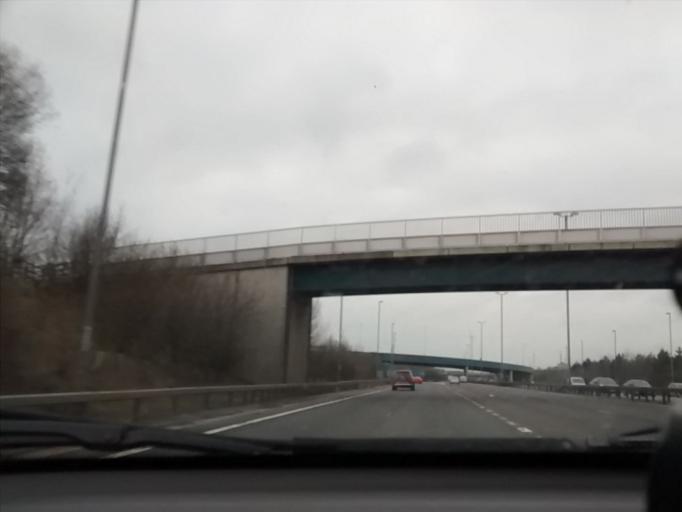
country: GB
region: England
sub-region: Essex
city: Stansted
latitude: 51.8786
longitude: 0.2034
